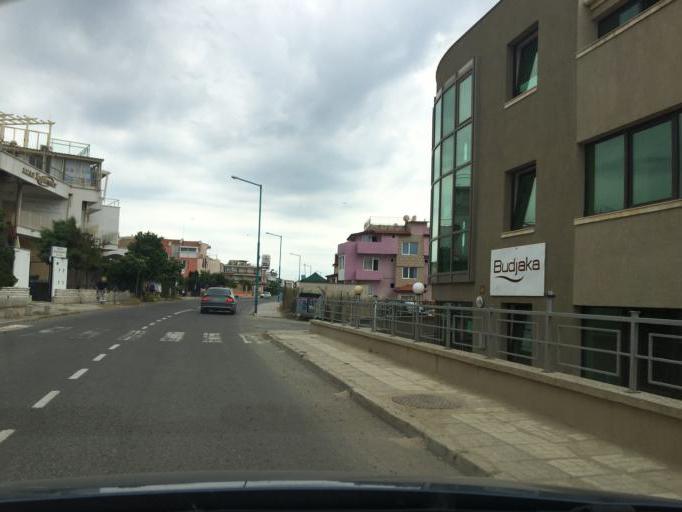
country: BG
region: Burgas
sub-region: Obshtina Sozopol
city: Sozopol
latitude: 42.4086
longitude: 27.7041
